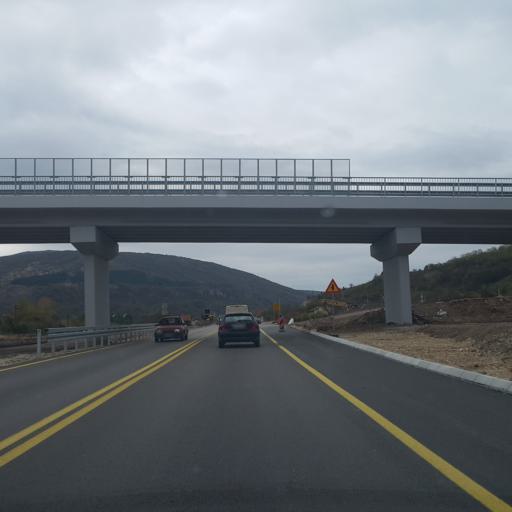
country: RS
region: Central Serbia
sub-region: Pirotski Okrug
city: Pirot
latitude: 43.2141
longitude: 22.5214
